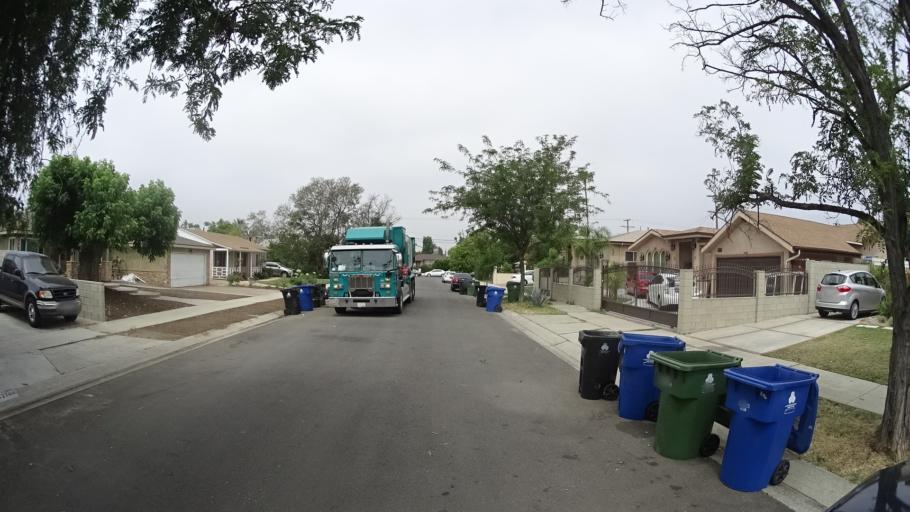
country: US
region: California
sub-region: Los Angeles County
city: North Hollywood
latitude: 34.1924
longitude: -118.4110
